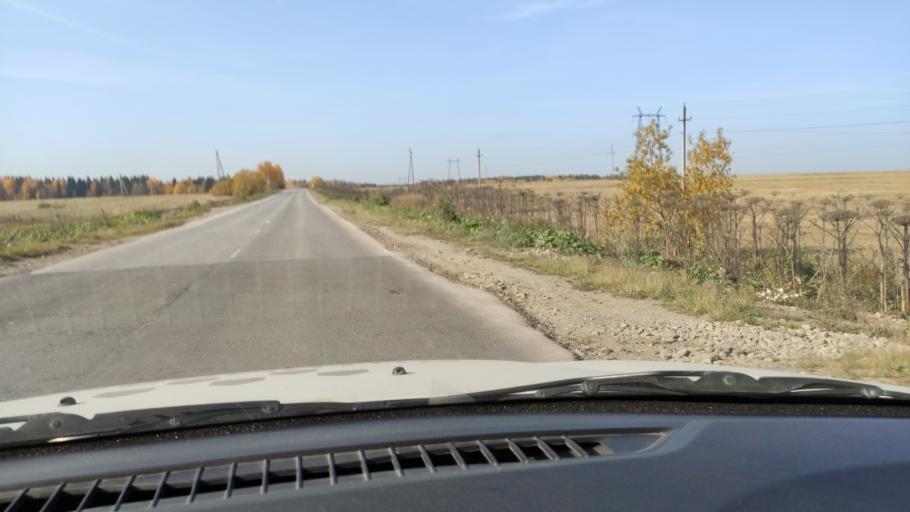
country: RU
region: Perm
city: Sylva
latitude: 58.0300
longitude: 56.6920
